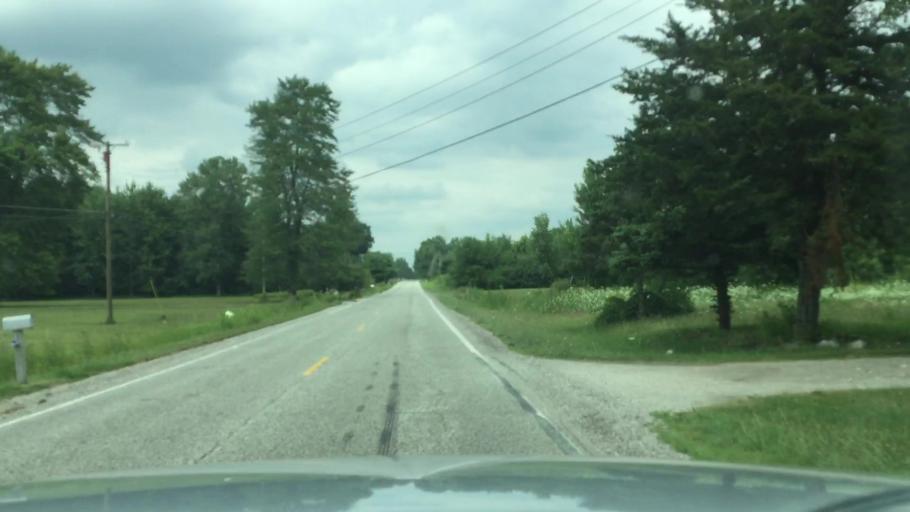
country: US
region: Michigan
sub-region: Saginaw County
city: Bridgeport
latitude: 43.3133
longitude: -83.8946
